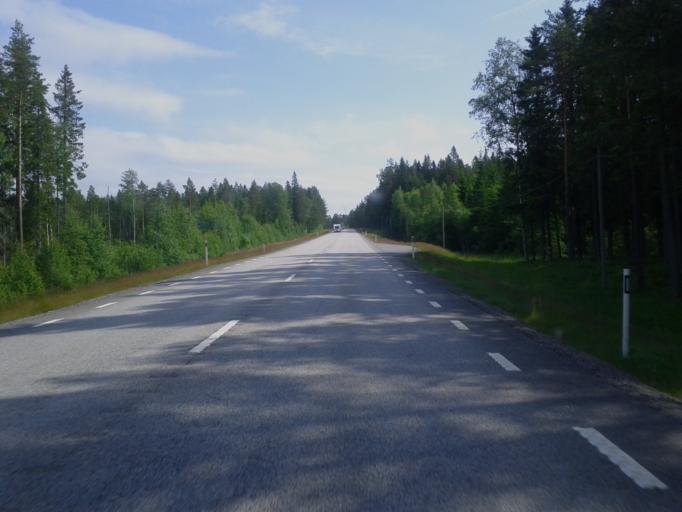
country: SE
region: Vaesterbotten
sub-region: Robertsfors Kommun
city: Robertsfors
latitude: 64.1808
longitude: 20.9757
